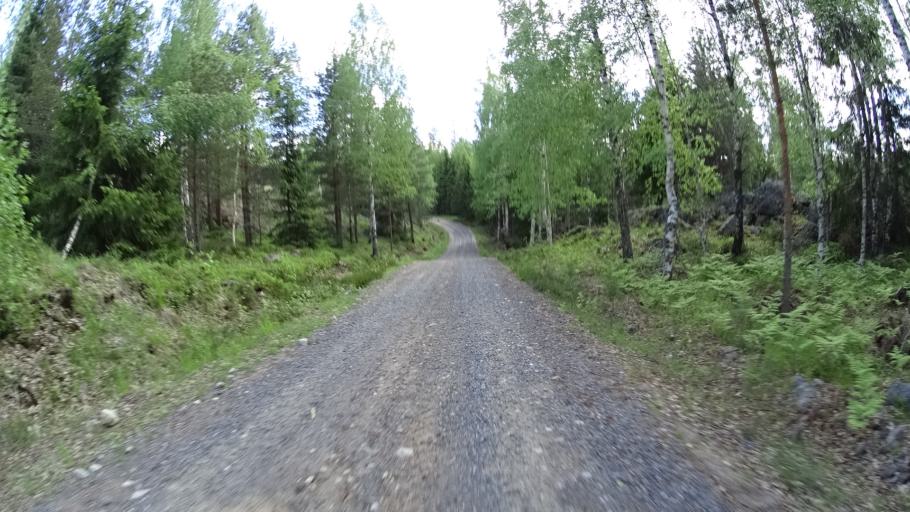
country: FI
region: Varsinais-Suomi
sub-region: Salo
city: Kisko
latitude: 60.1894
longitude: 23.5523
